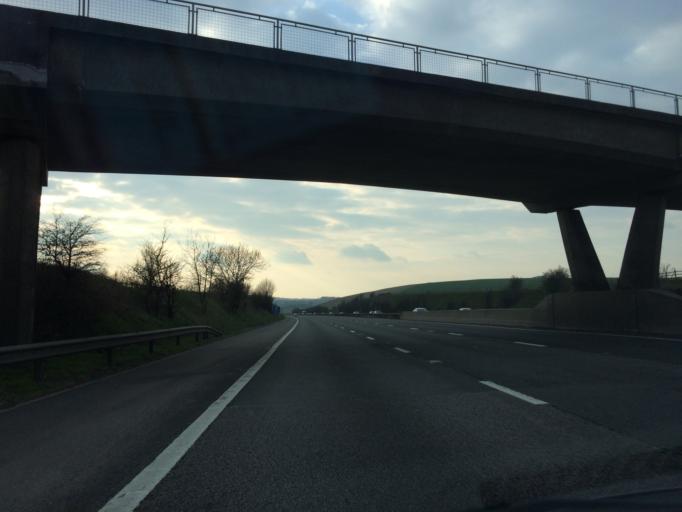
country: GB
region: England
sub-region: Wiltshire
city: Aldbourne
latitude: 51.5128
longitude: -1.6287
